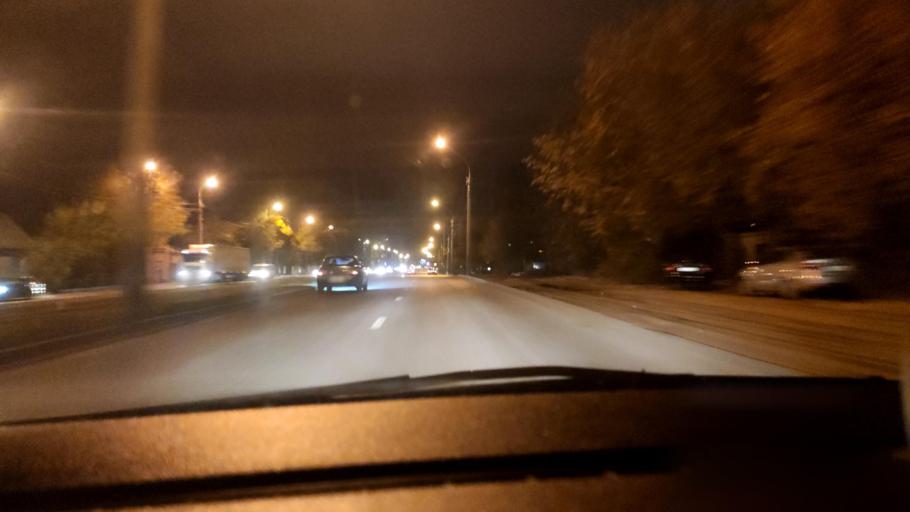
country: RU
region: Voronezj
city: Voronezh
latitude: 51.6367
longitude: 39.1694
